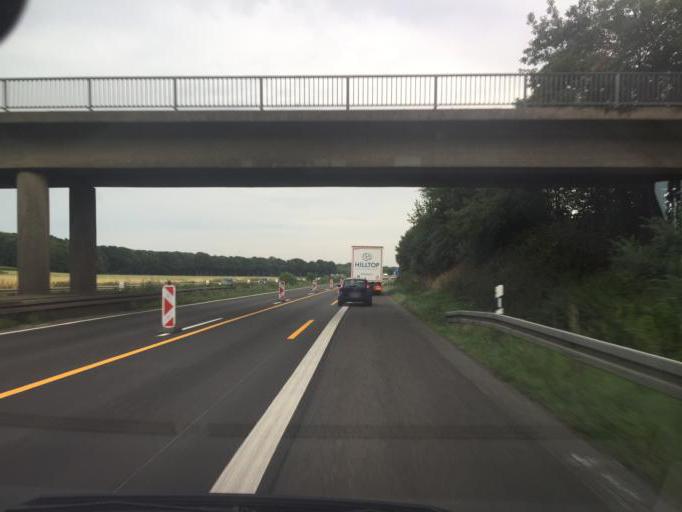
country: DE
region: North Rhine-Westphalia
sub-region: Regierungsbezirk Dusseldorf
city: Viersen
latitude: 51.2671
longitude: 6.3571
